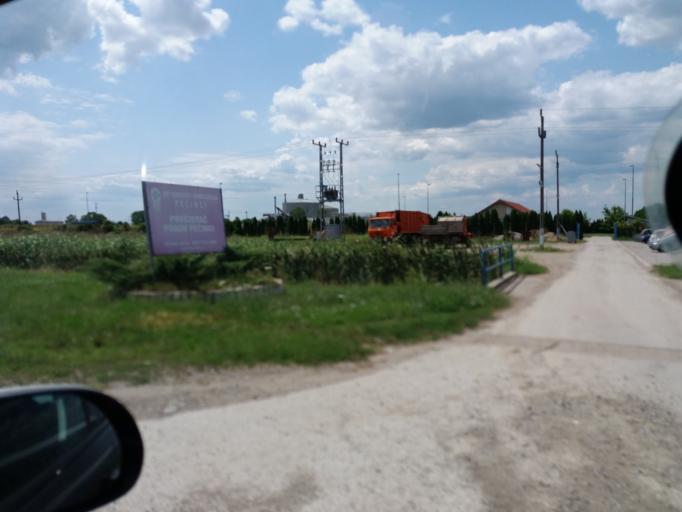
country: RS
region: Autonomna Pokrajina Vojvodina
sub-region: Sremski Okrug
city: Pecinci
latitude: 44.8892
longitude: 19.9632
